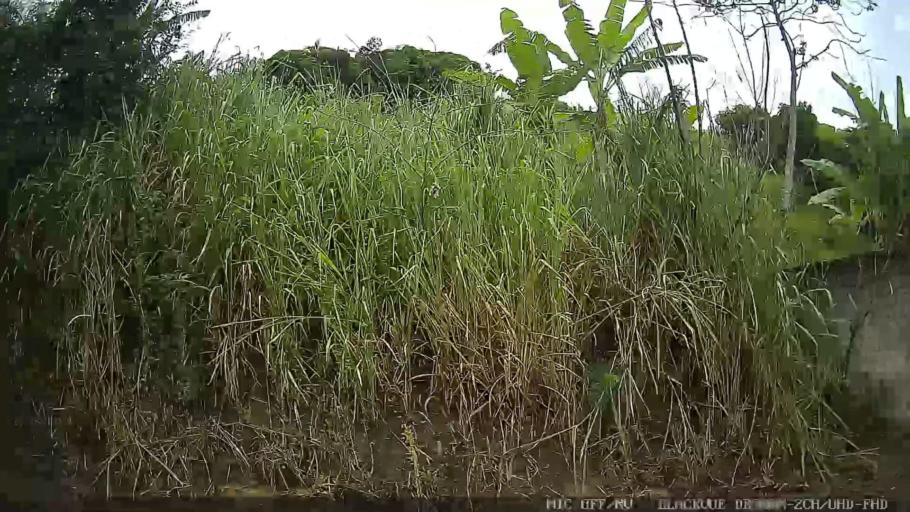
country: BR
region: Sao Paulo
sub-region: Sao Sebastiao
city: Sao Sebastiao
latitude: -23.7258
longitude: -45.4330
